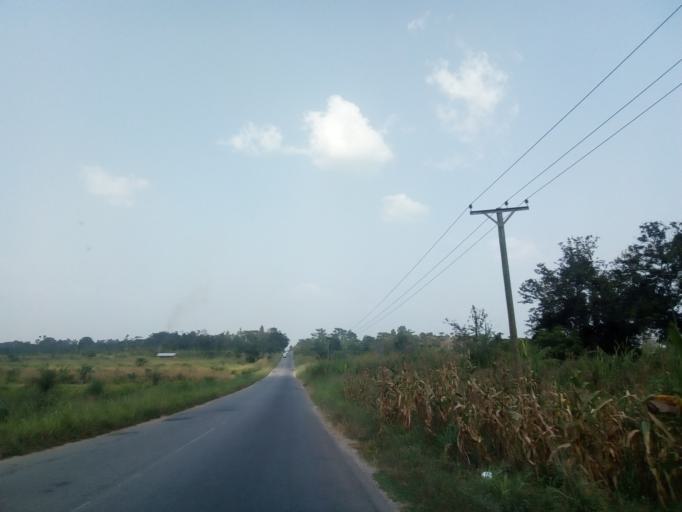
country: GH
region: Eastern
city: Suhum
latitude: 6.0520
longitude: -0.4072
